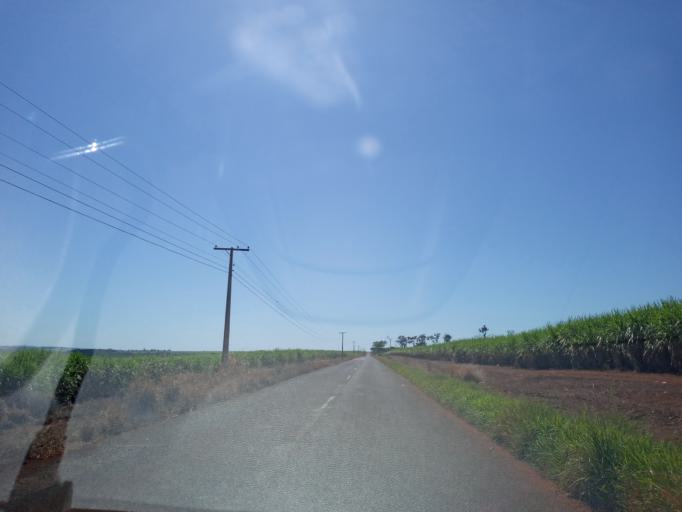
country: BR
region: Goias
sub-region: Itumbiara
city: Itumbiara
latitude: -18.4263
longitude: -49.1791
